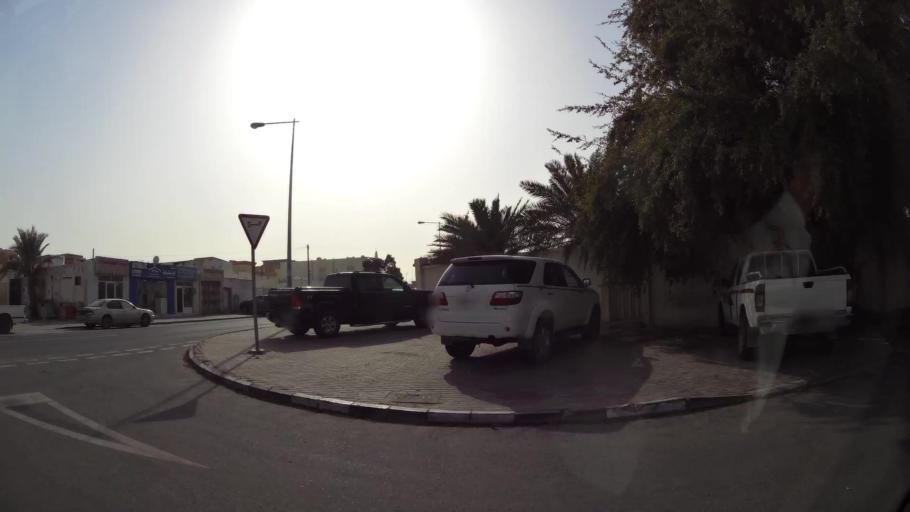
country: QA
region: Baladiyat ar Rayyan
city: Ar Rayyan
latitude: 25.2391
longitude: 51.4381
